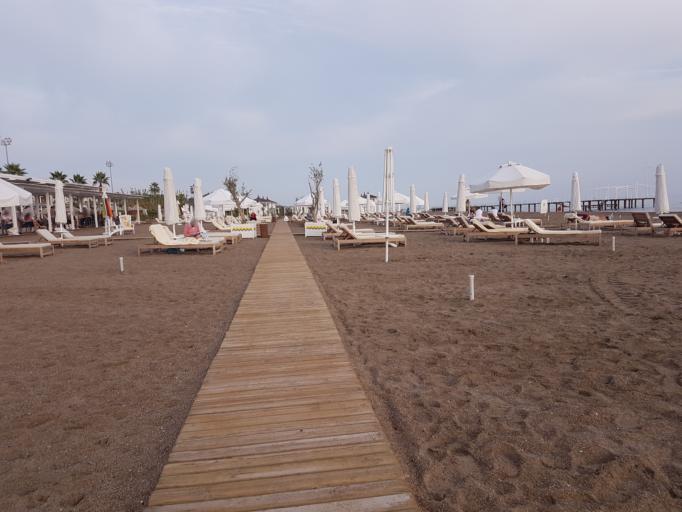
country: TR
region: Antalya
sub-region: Serik
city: Kumkoey
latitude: 36.8517
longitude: 30.8560
